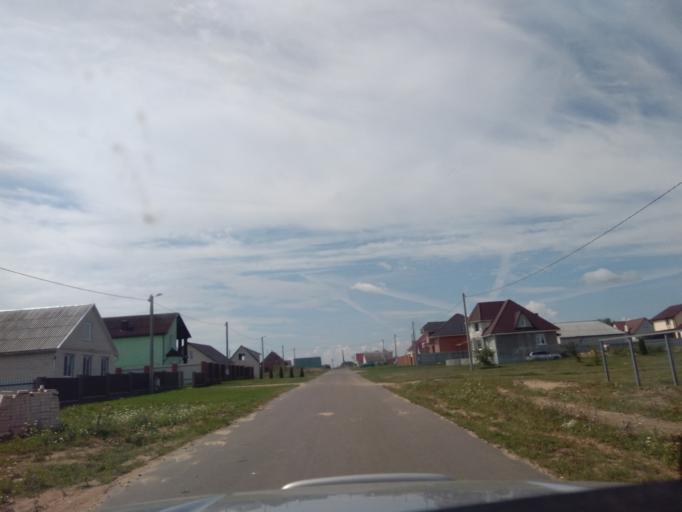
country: BY
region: Minsk
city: Kapyl'
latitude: 53.1617
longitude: 27.1001
